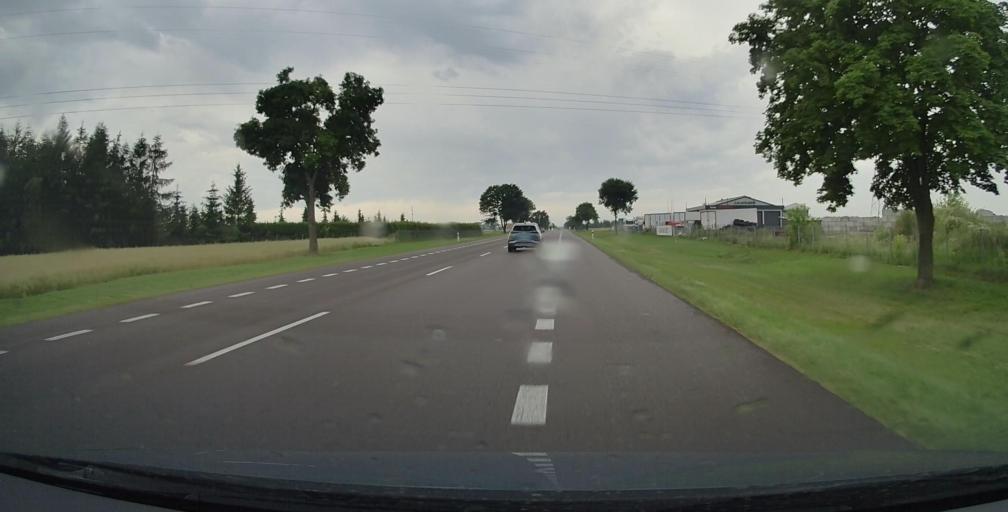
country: PL
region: Lublin Voivodeship
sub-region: Powiat bialski
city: Miedzyrzec Podlaski
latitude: 51.9999
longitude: 22.7990
